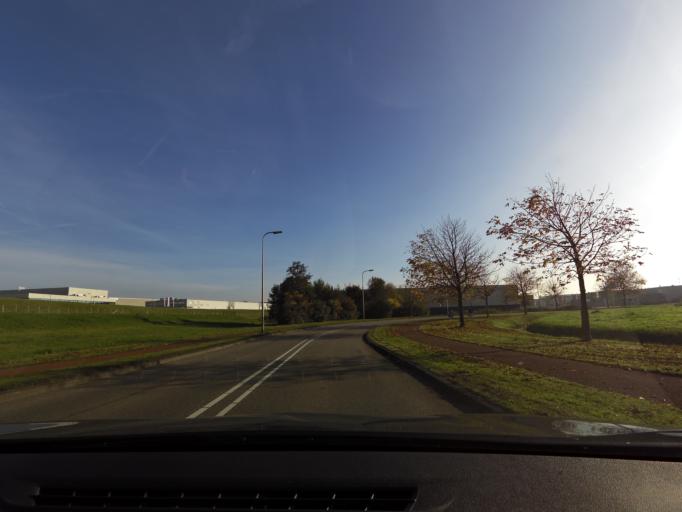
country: NL
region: South Holland
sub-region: Gemeente Ridderkerk
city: Ridderkerk
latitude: 51.8833
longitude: 4.6174
